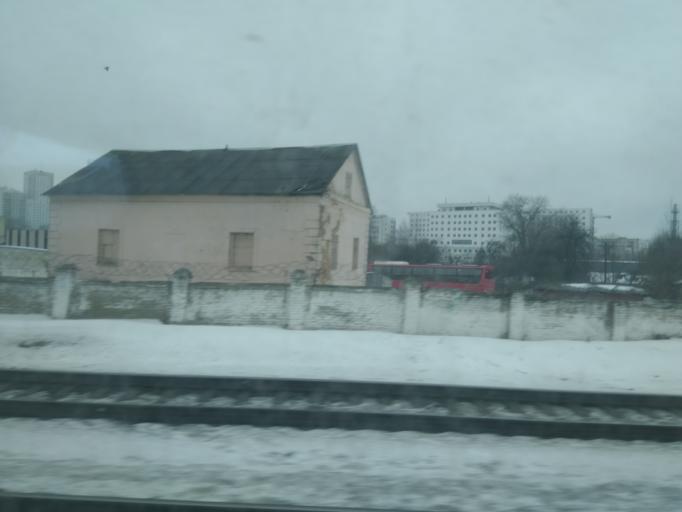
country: BY
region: Minsk
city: Minsk
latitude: 53.8898
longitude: 27.5320
